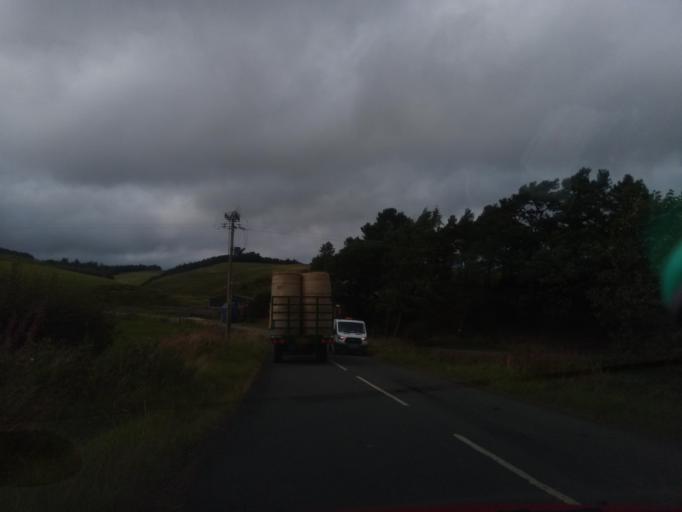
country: GB
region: Scotland
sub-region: The Scottish Borders
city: Duns
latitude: 55.8335
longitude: -2.4356
